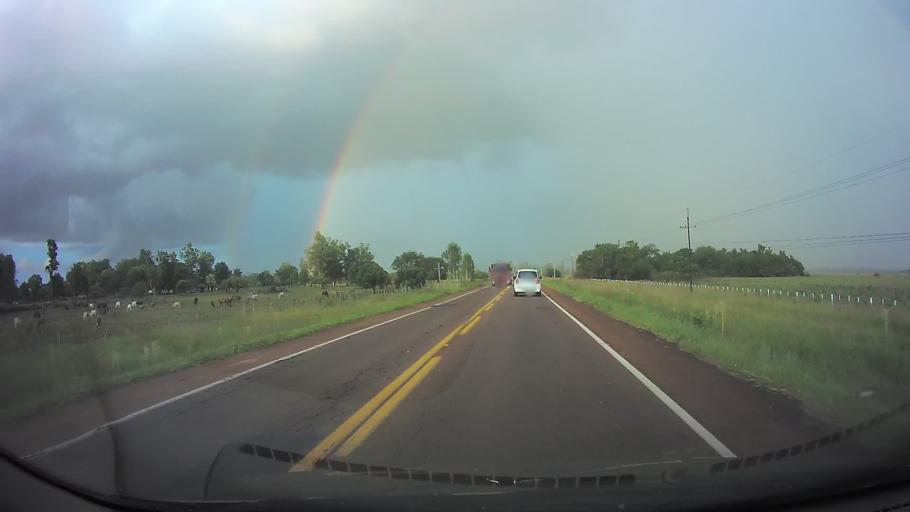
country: PY
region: Paraguari
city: Carapegua
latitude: -25.7115
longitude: -57.1905
